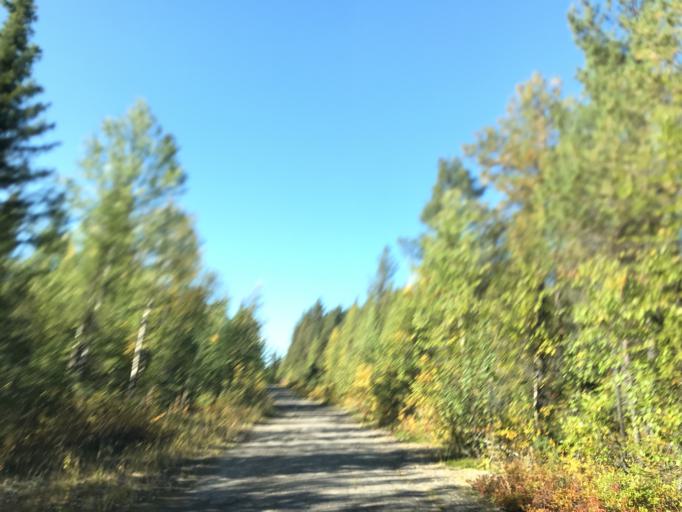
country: SE
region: Norrbotten
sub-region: Gallivare Kommun
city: Malmberget
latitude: 67.6469
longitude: 21.1008
